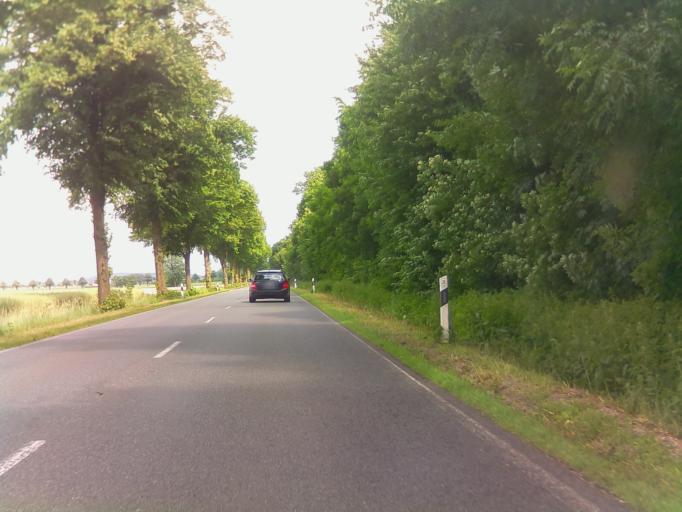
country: DE
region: Lower Saxony
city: Springe
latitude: 52.1759
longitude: 9.6200
